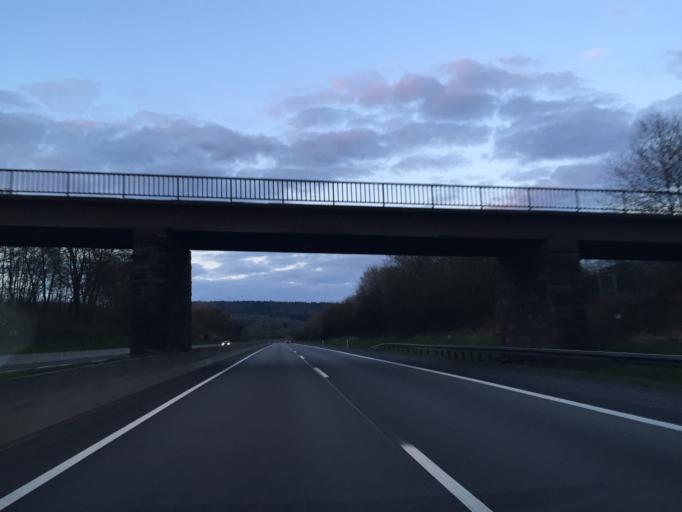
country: DE
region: Thuringia
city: Lauchroden
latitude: 51.0136
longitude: 10.1106
